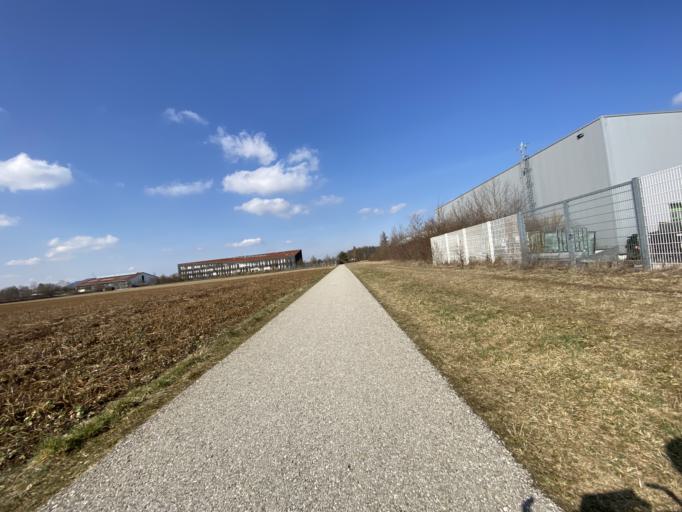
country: DE
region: Bavaria
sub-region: Upper Bavaria
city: Aschheim
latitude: 48.1640
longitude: 11.7283
